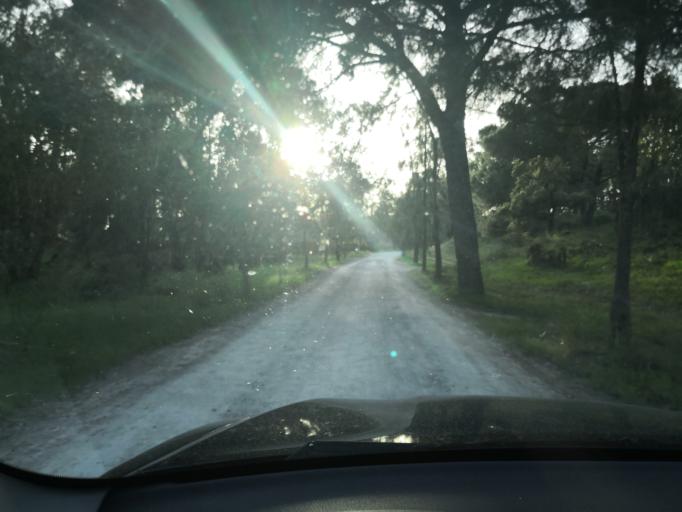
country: PT
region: Setubal
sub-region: Setubal
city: Setubal
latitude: 38.5290
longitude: -8.8071
